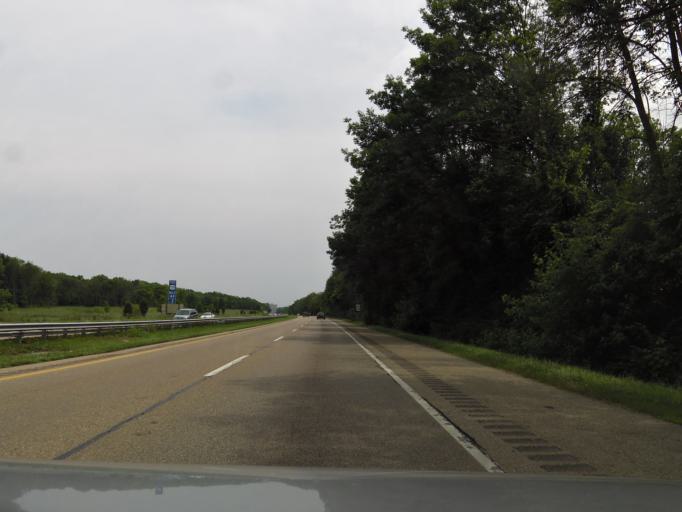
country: US
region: Ohio
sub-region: Greene County
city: Beavercreek
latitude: 39.7167
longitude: -84.0525
